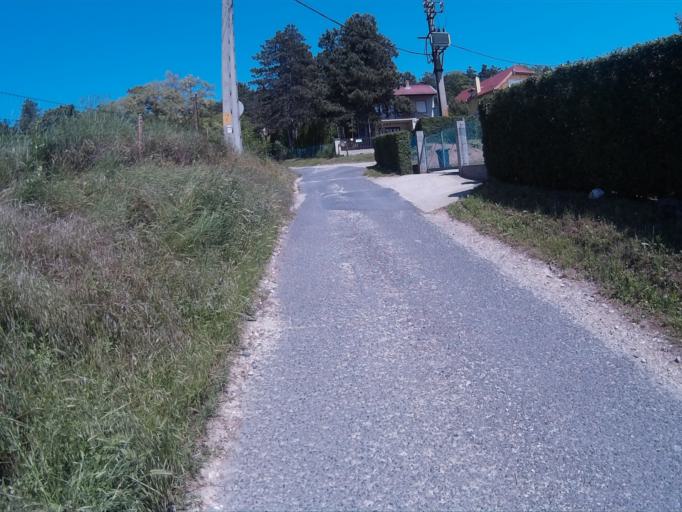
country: HU
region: Zala
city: Gyenesdias
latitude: 46.7767
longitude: 17.2893
